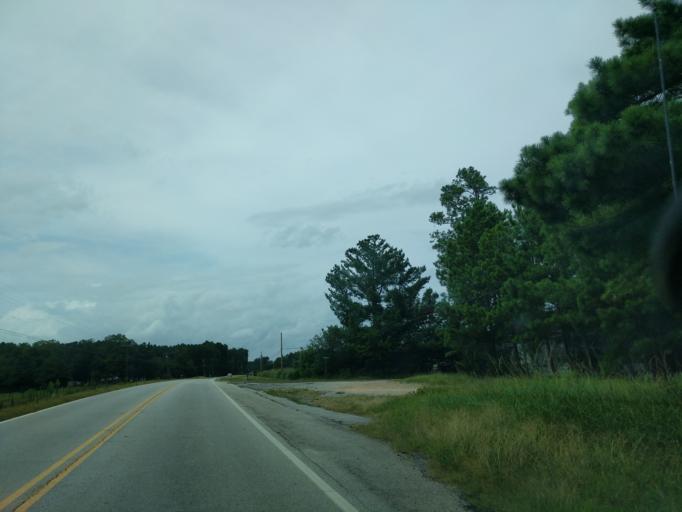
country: US
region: Georgia
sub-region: Elbert County
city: Elberton
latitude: 34.0615
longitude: -82.8309
